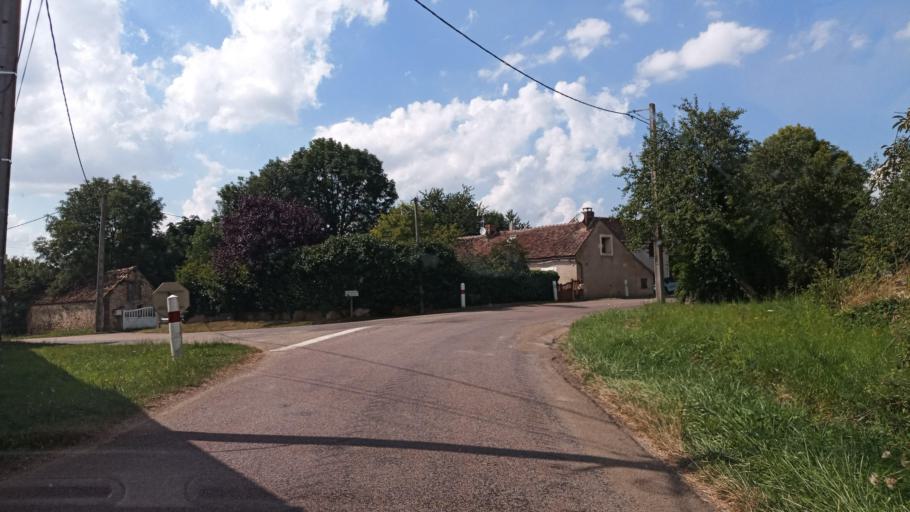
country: FR
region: Bourgogne
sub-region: Departement de l'Yonne
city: Egriselles-le-Bocage
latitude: 48.0390
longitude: 3.1590
